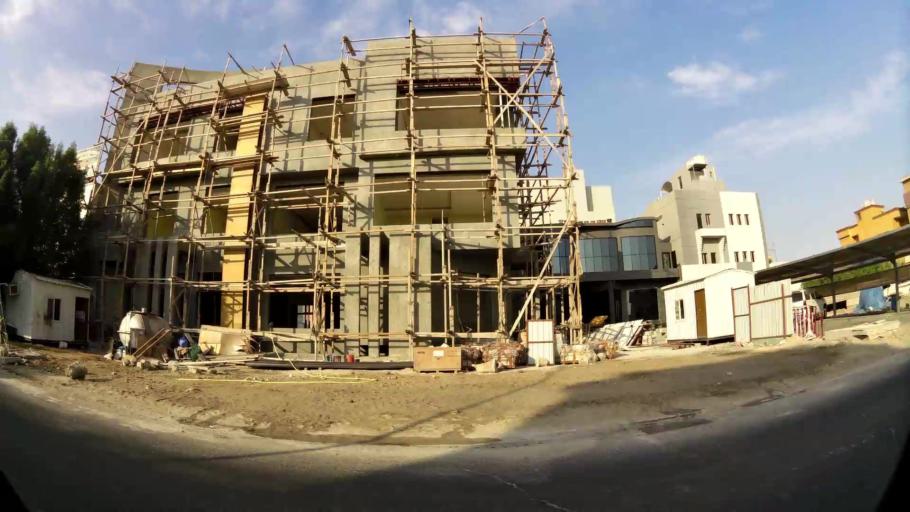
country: KW
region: Muhafazat Hawalli
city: Ar Rumaythiyah
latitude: 29.3211
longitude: 48.0726
